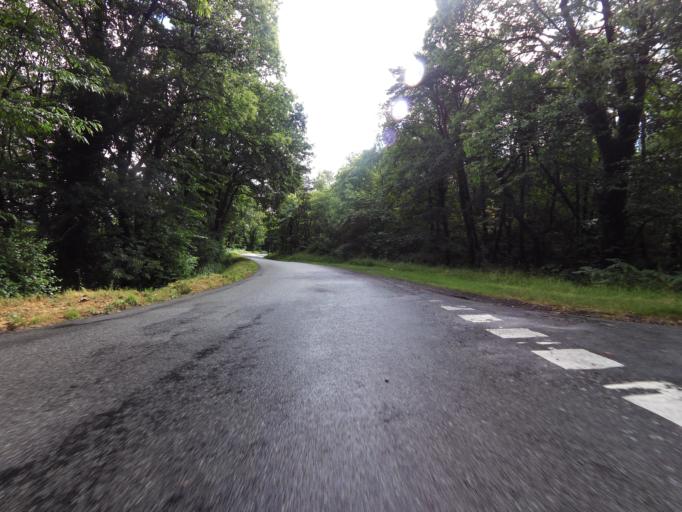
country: FR
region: Brittany
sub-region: Departement du Morbihan
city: Malansac
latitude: 47.7026
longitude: -2.3004
